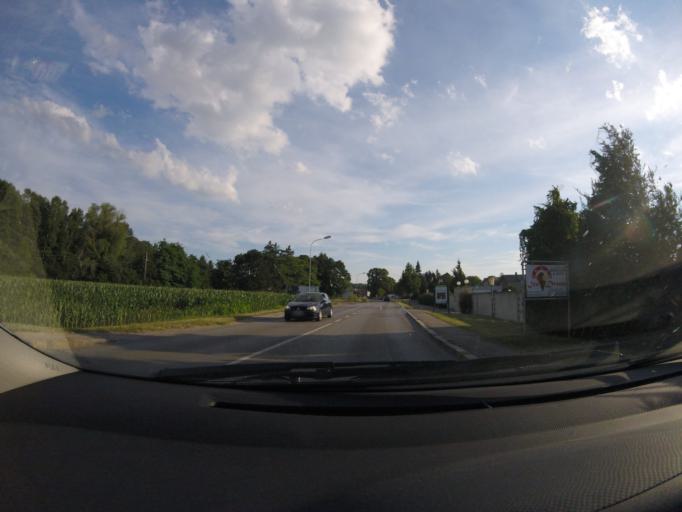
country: AT
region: Lower Austria
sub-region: Politischer Bezirk Wiener Neustadt
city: Zillingdorf
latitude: 47.8615
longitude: 16.3247
